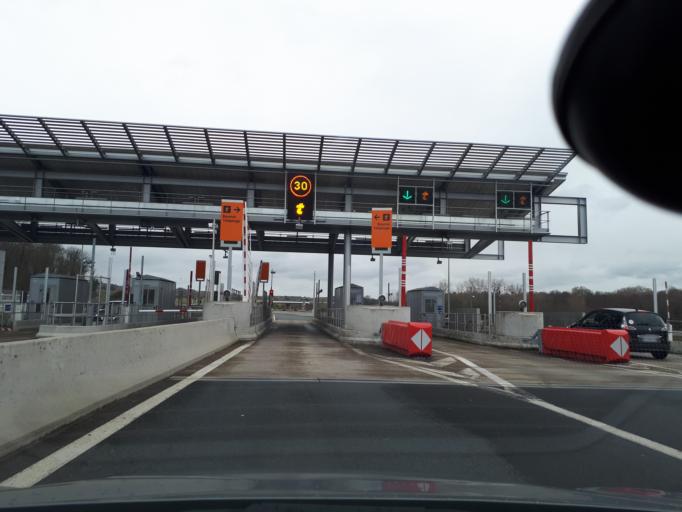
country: FR
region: Rhone-Alpes
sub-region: Departement du Rhone
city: Saint-Romain-de-Popey
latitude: 45.8764
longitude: 4.5217
